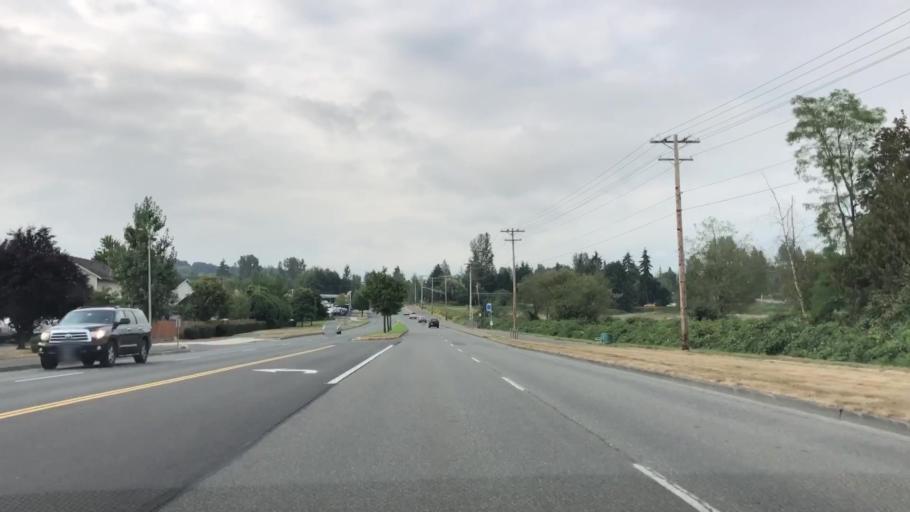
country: US
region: Washington
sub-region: Snohomish County
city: Monroe
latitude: 47.8522
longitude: -122.0120
